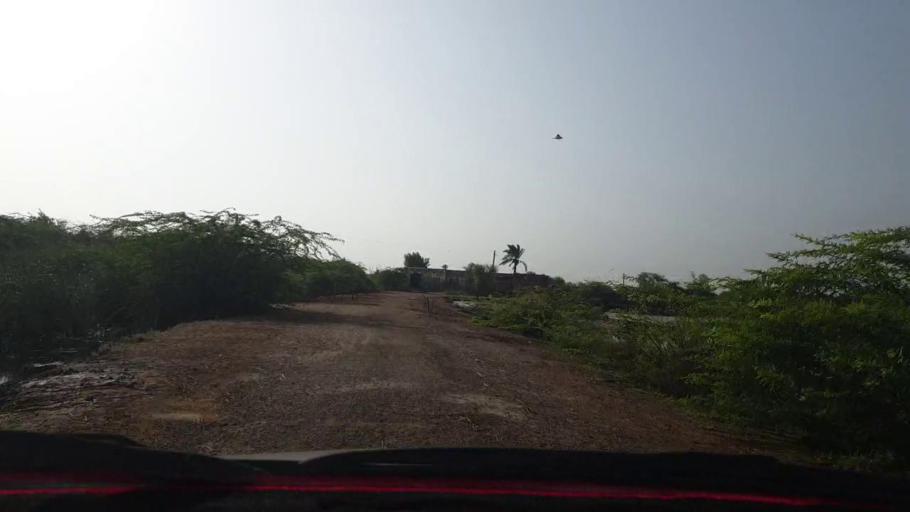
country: PK
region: Sindh
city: Talhar
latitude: 24.9252
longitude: 68.7510
